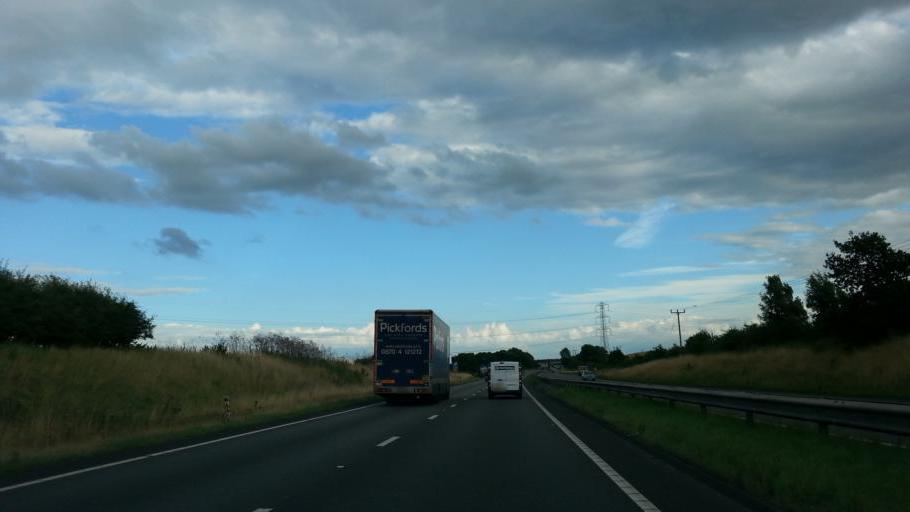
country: GB
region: England
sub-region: Nottinghamshire
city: Tuxford
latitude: 53.1883
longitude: -0.8308
